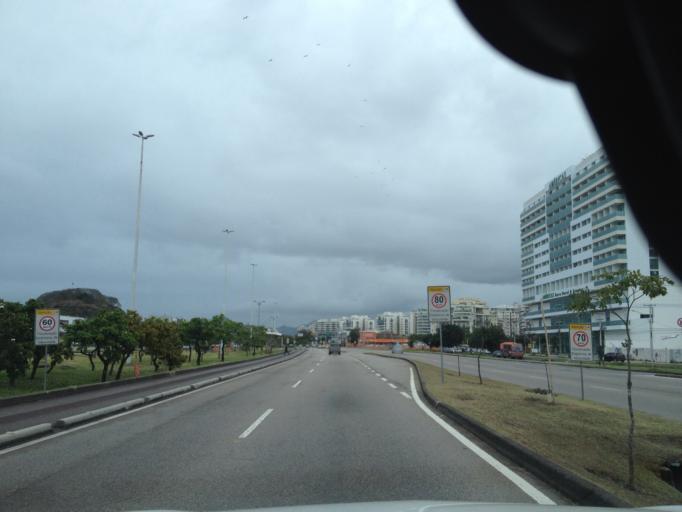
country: BR
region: Rio de Janeiro
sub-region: Nilopolis
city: Nilopolis
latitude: -23.0001
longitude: -43.4143
